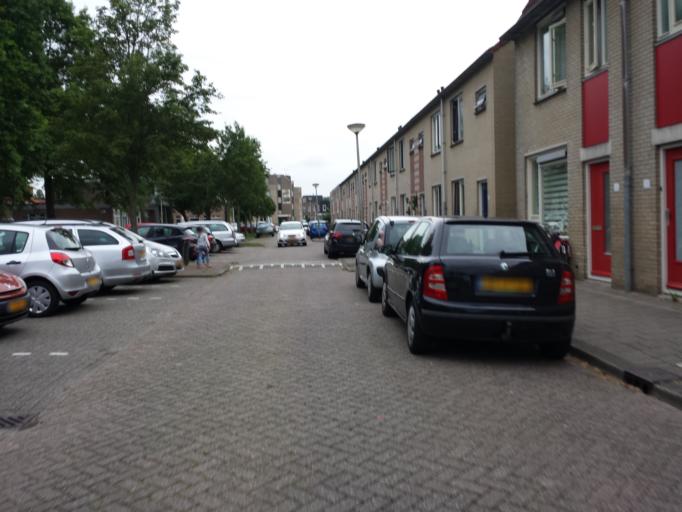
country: NL
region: South Holland
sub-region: Gemeente Gouda
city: Gouda
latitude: 52.0062
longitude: 4.7055
